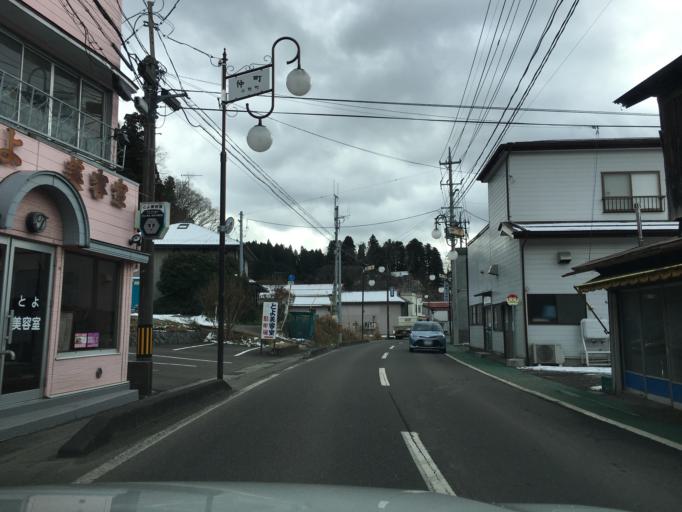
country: JP
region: Fukushima
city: Funehikimachi-funehiki
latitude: 37.2880
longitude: 140.6275
